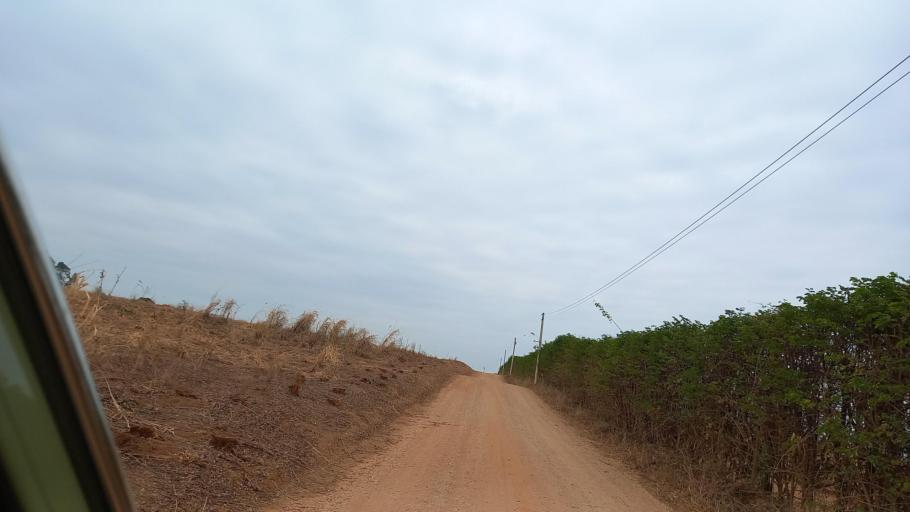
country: BR
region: Sao Paulo
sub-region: Moji-Guacu
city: Mogi-Gaucu
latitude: -22.2776
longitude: -46.8449
